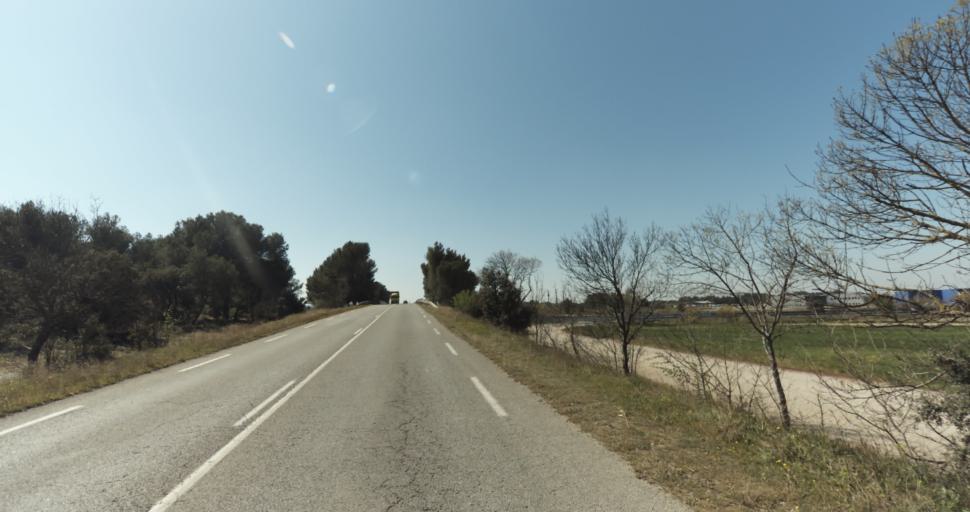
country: FR
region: Provence-Alpes-Cote d'Azur
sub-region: Departement des Bouches-du-Rhone
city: Pelissanne
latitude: 43.6177
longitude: 5.1411
